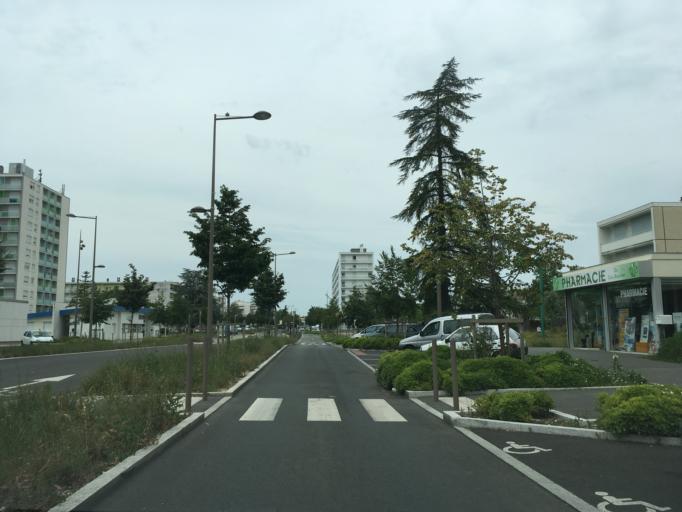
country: FR
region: Poitou-Charentes
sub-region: Departement des Deux-Sevres
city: Niort
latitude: 46.3143
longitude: -0.4815
